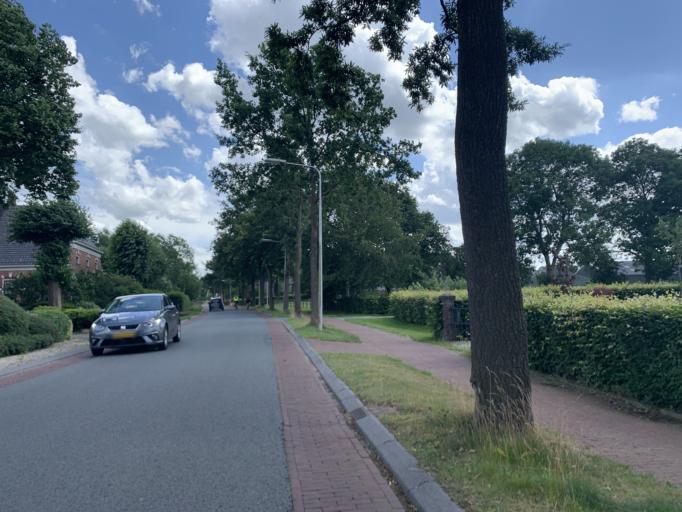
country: NL
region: Groningen
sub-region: Gemeente Haren
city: Haren
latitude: 53.1602
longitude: 6.6384
